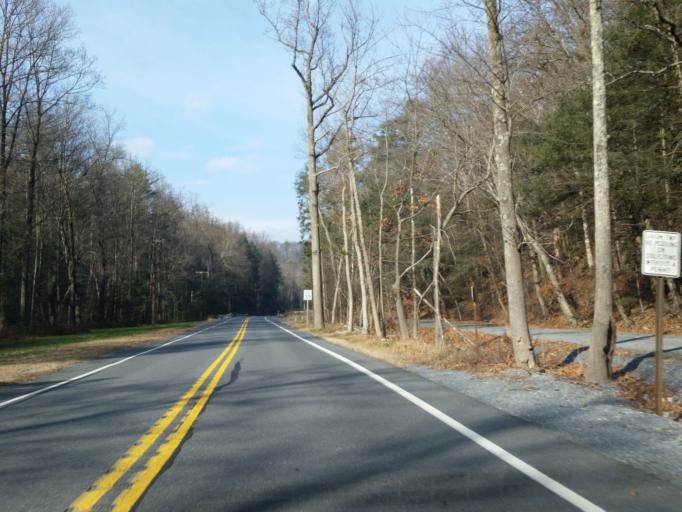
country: US
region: Pennsylvania
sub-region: Lebanon County
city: Jonestown
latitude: 40.4421
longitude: -76.6002
